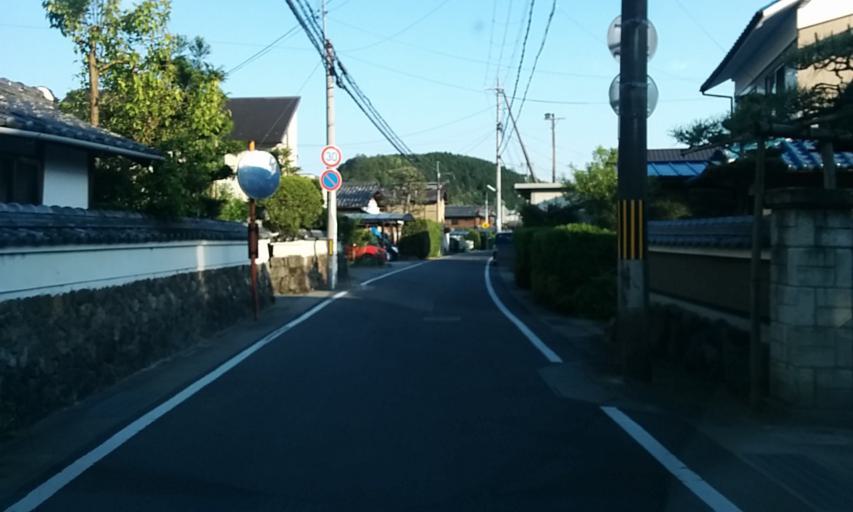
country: JP
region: Kyoto
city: Kameoka
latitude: 35.0908
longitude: 135.5101
